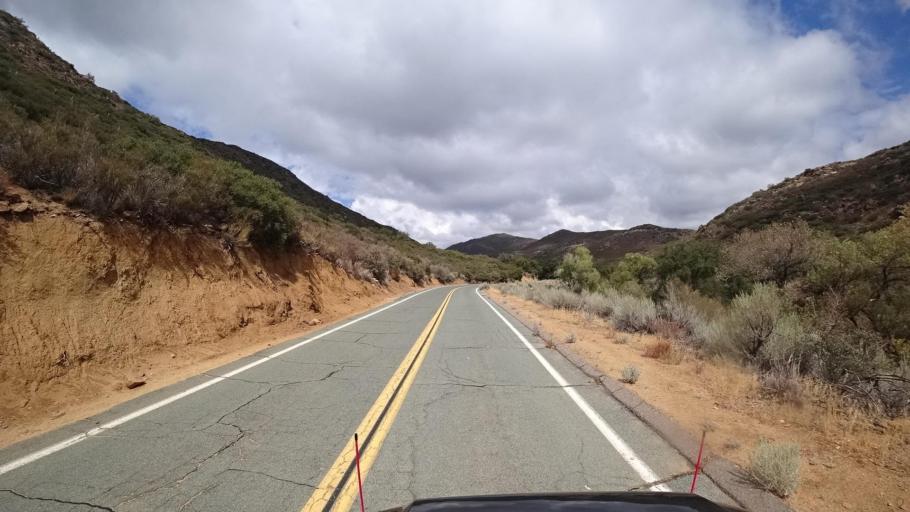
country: US
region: California
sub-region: San Diego County
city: Pine Valley
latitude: 32.7735
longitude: -116.4507
